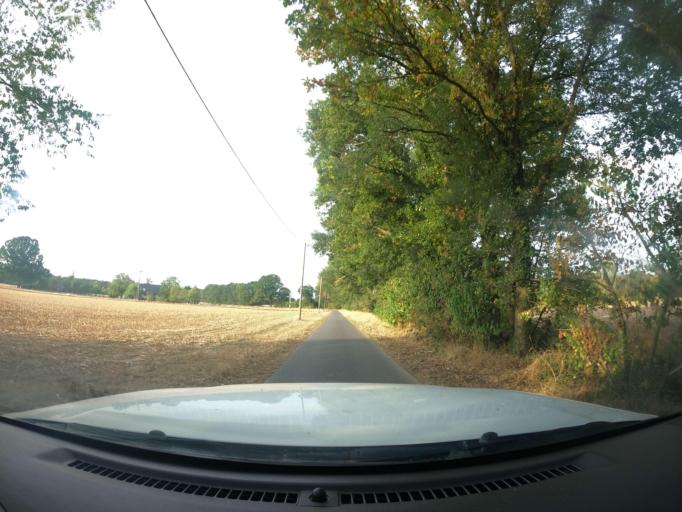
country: DE
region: North Rhine-Westphalia
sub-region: Regierungsbezirk Dusseldorf
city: Hamminkeln
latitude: 51.7026
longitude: 6.5731
